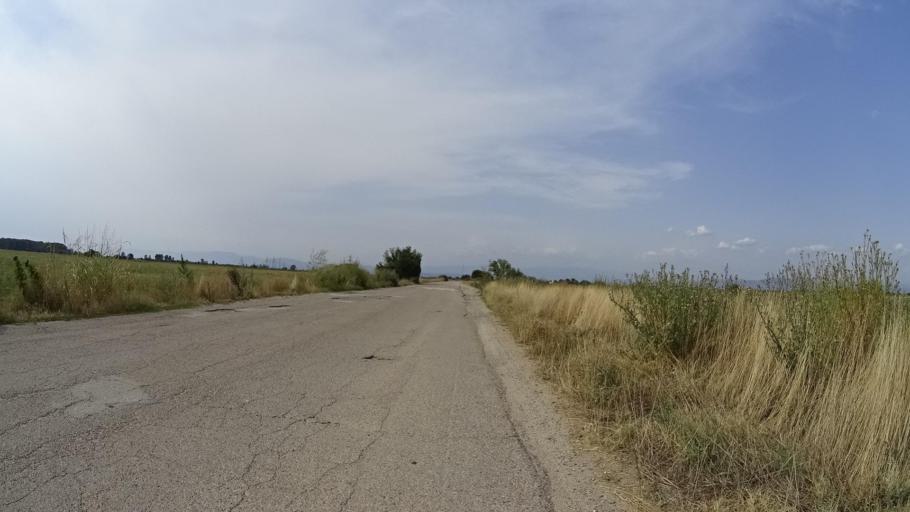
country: BG
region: Plovdiv
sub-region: Obshtina Kaloyanovo
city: Kaloyanovo
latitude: 42.3159
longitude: 24.7994
